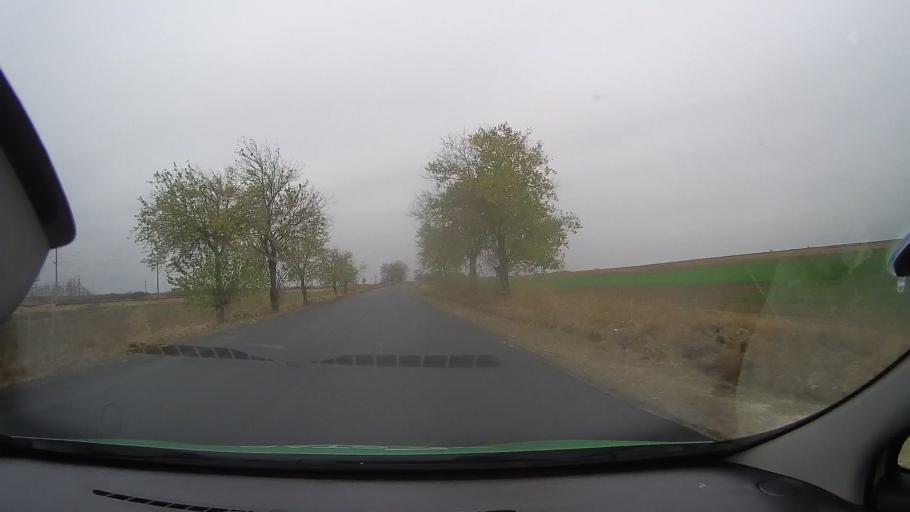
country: RO
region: Ialomita
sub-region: Comuna Valea Ciorii
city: Valea Ciorii
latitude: 44.6987
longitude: 27.5990
